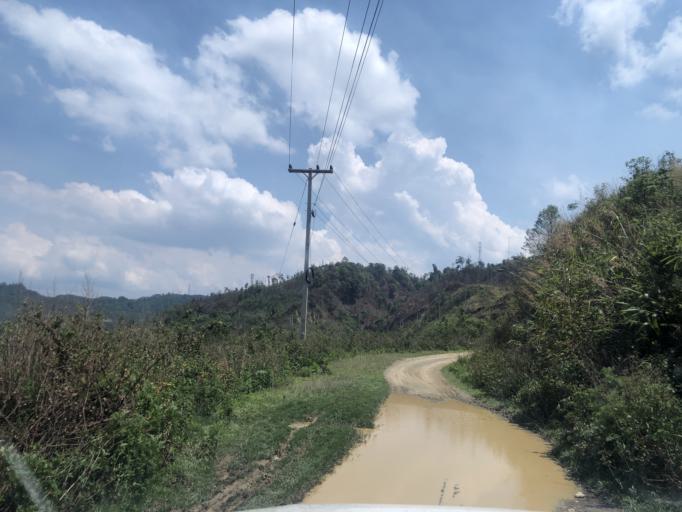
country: LA
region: Phongsali
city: Phongsali
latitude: 21.4024
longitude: 102.1888
